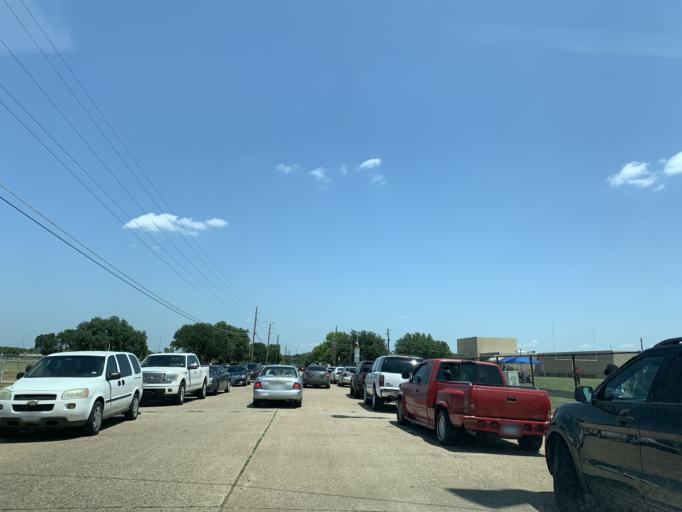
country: US
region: Texas
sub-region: Dallas County
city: Hutchins
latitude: 32.6925
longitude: -96.7680
